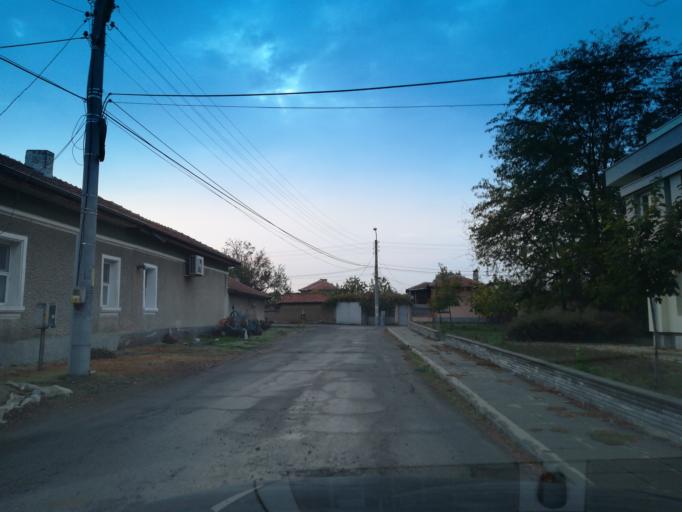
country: BG
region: Stara Zagora
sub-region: Obshtina Chirpan
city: Chirpan
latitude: 42.1748
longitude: 25.2087
